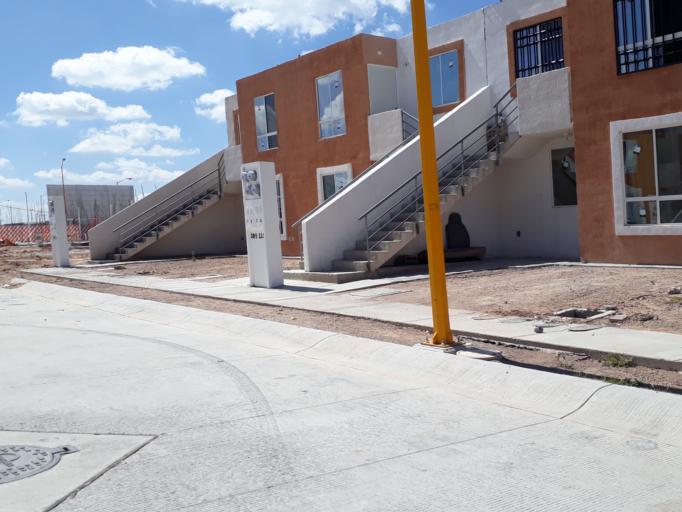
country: MX
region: Aguascalientes
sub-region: Aguascalientes
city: San Sebastian [Fraccionamiento]
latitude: 21.8073
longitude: -102.2760
